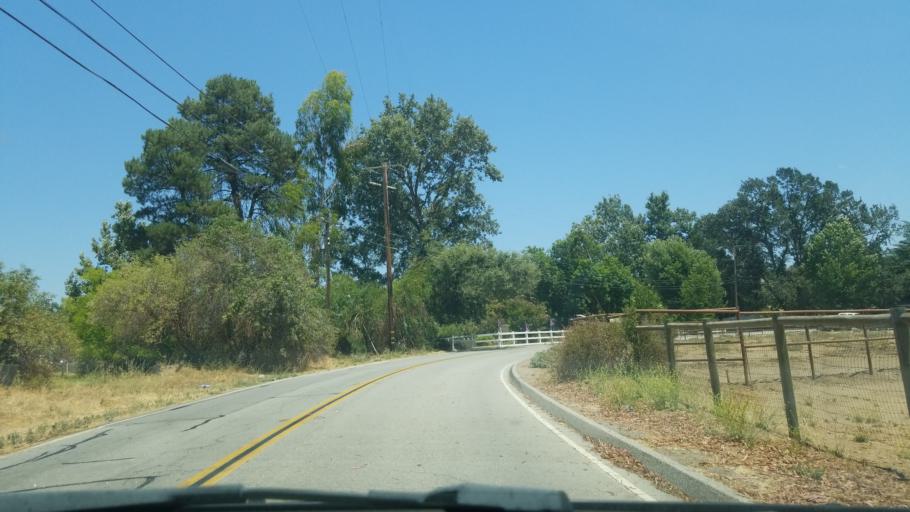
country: US
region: California
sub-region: San Luis Obispo County
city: Atascadero
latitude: 35.4966
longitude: -120.6504
